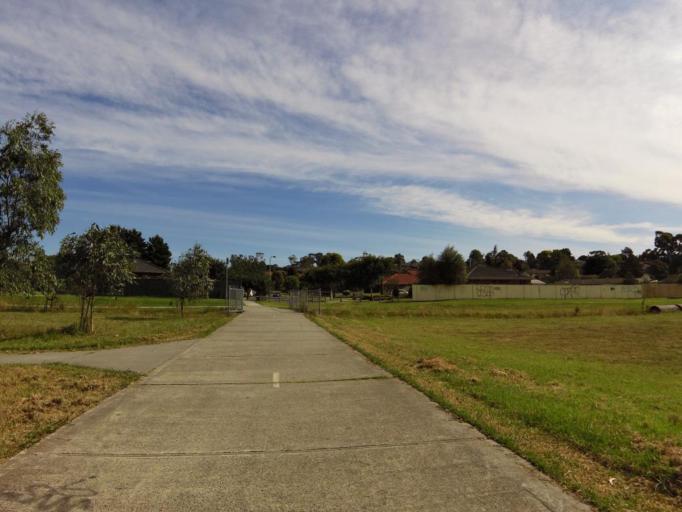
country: AU
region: Victoria
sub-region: Casey
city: Eumemmerring
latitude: -37.9959
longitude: 145.2606
